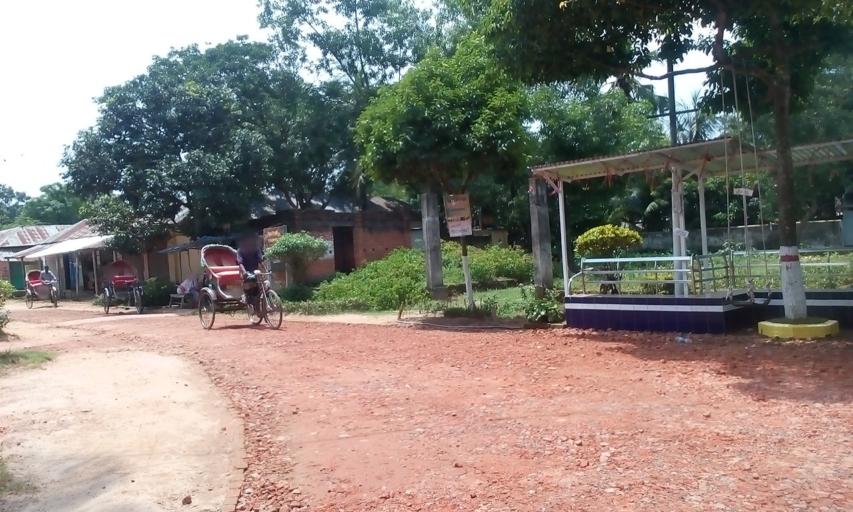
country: BD
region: Rangpur Division
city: Parbatipur
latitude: 25.3994
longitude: 88.9909
